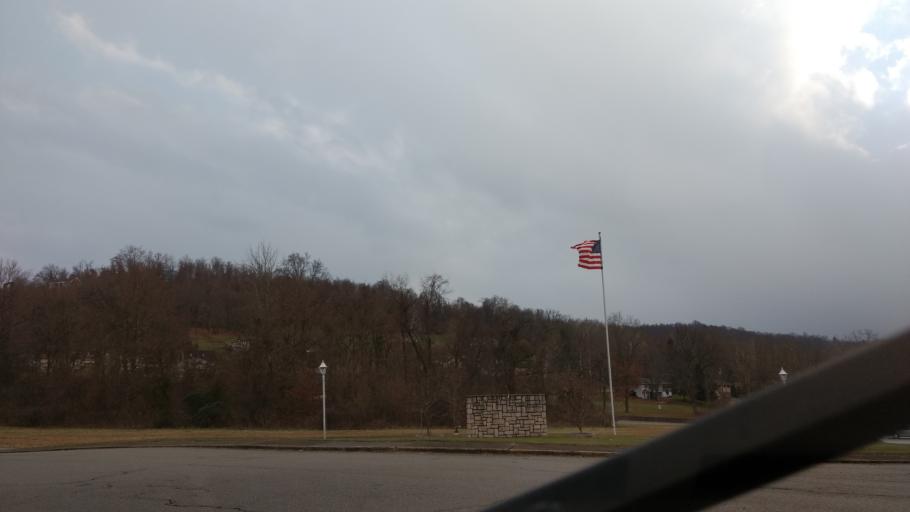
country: US
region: Pennsylvania
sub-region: Washington County
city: Speers
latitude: 40.1203
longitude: -79.8864
